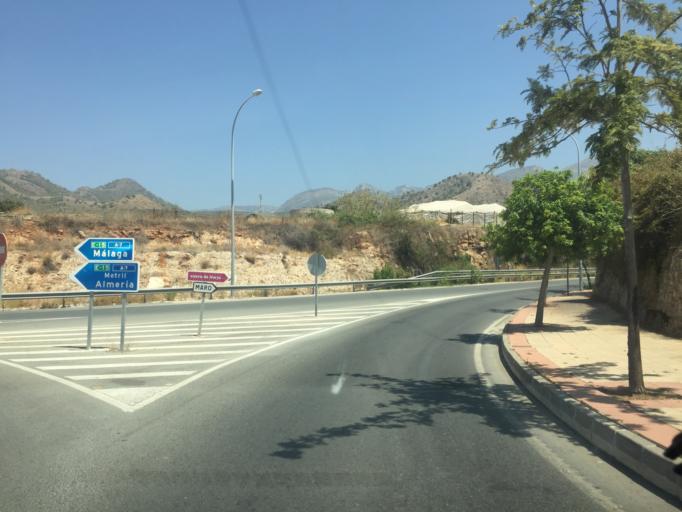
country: ES
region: Andalusia
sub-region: Provincia de Malaga
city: Nerja
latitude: 36.7559
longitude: -3.8514
